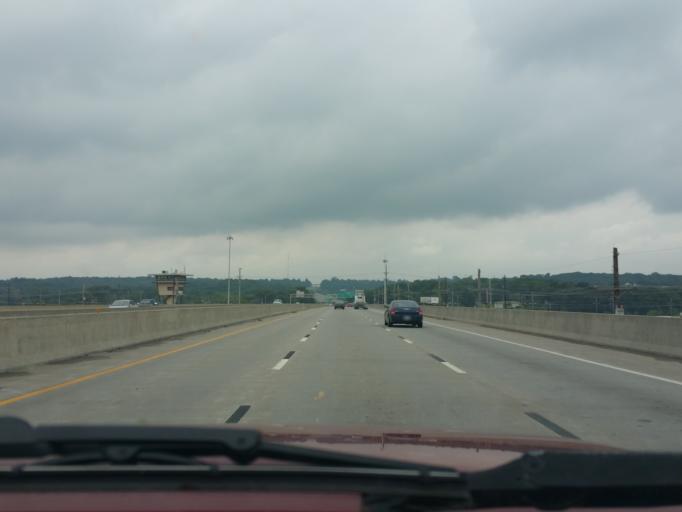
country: US
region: Kansas
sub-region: Johnson County
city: Shawnee
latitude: 39.0857
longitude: -94.6807
